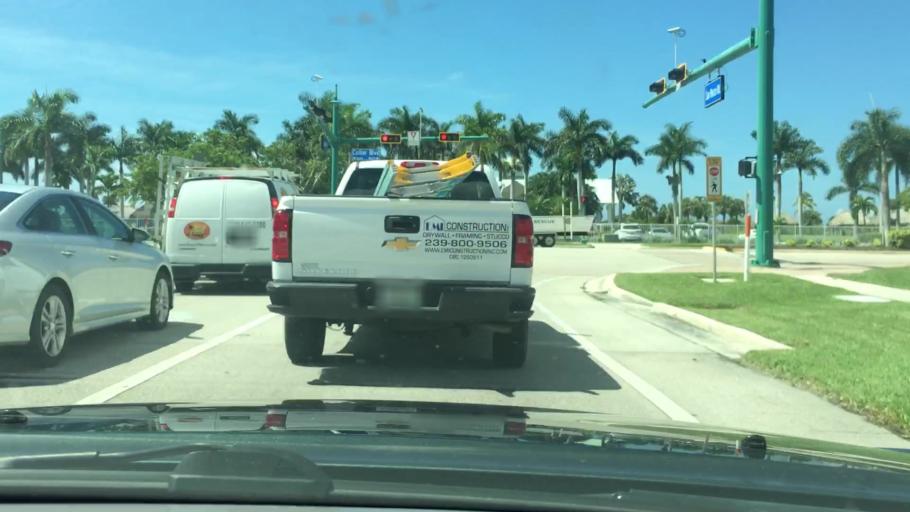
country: US
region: Florida
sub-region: Collier County
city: Marco
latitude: 25.9364
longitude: -81.7313
